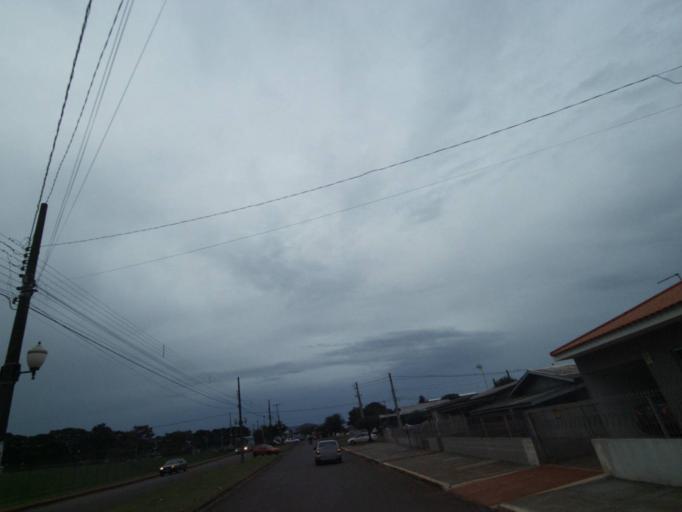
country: BR
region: Parana
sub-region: Campo Mourao
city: Campo Mourao
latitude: -24.0218
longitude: -52.3558
